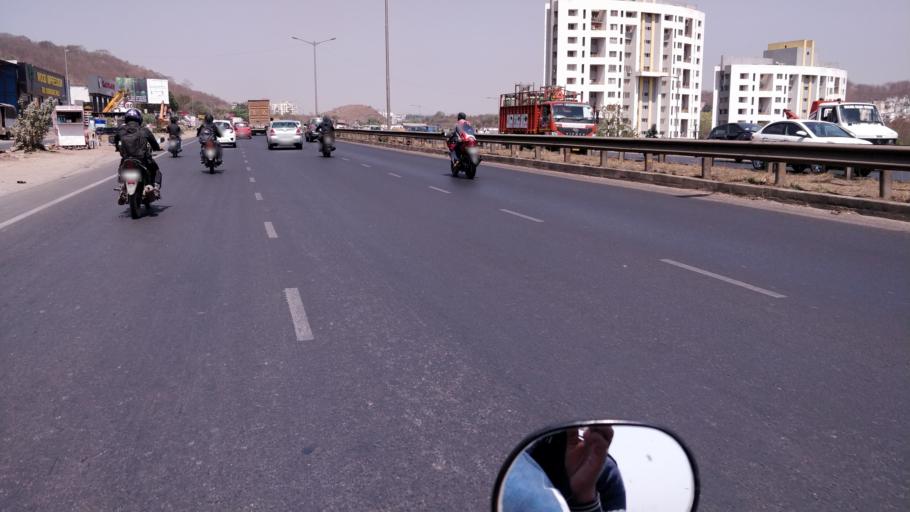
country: IN
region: Maharashtra
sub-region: Pune Division
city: Shivaji Nagar
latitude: 18.5409
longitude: 73.7790
